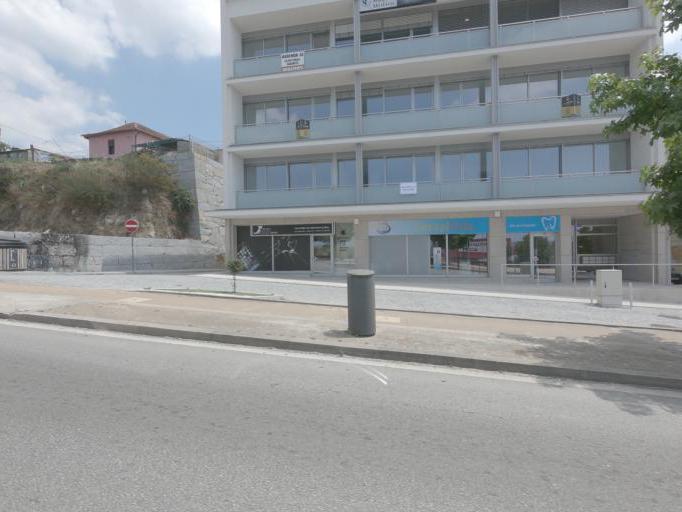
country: PT
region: Porto
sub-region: Penafiel
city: Penafiel
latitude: 41.1948
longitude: -8.2965
